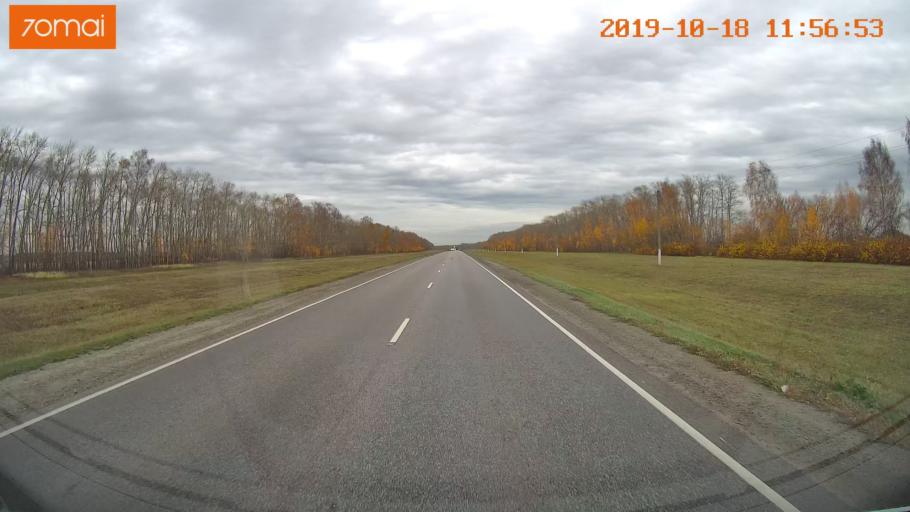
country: RU
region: Rjazan
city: Mikhaylov
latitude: 54.2660
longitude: 39.1280
